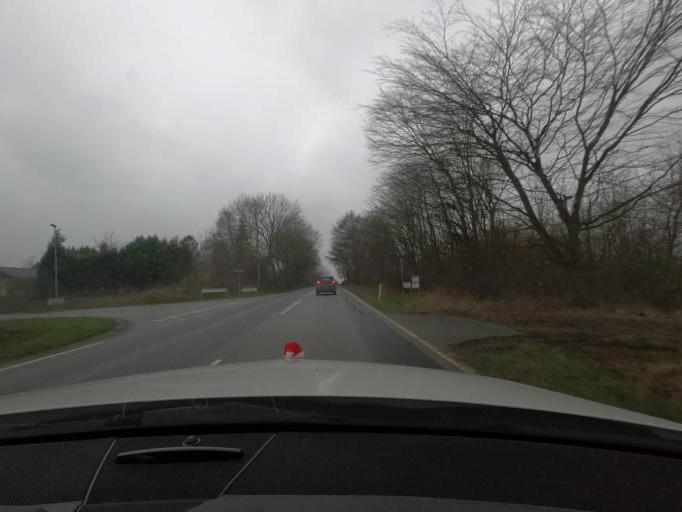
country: DK
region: South Denmark
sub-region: Haderslev Kommune
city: Starup
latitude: 55.1940
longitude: 9.5210
